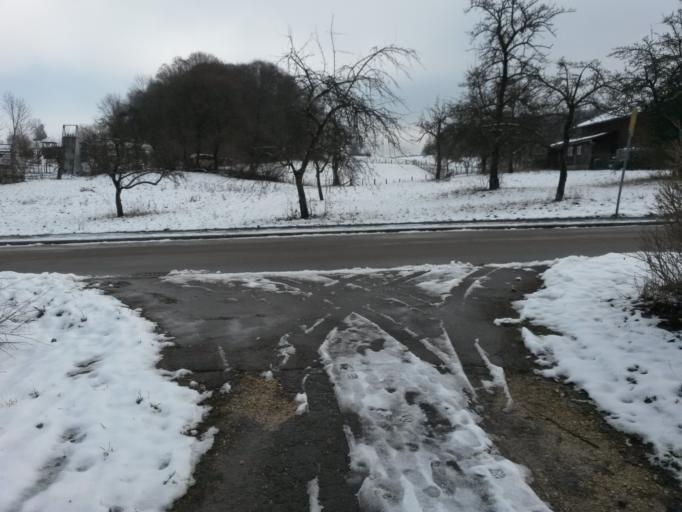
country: DE
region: Baden-Wuerttemberg
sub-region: Regierungsbezirk Stuttgart
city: Geislingen an der Steige
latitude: 48.6121
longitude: 9.8562
